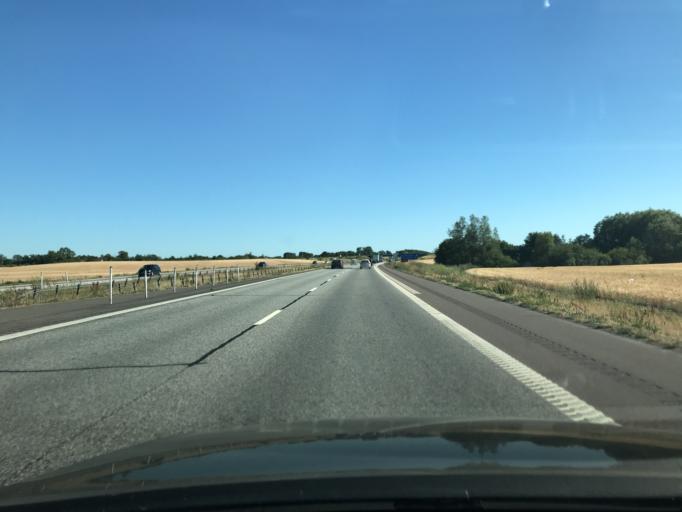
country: SE
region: Skane
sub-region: Burlovs Kommun
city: Arloev
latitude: 55.5957
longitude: 13.1170
